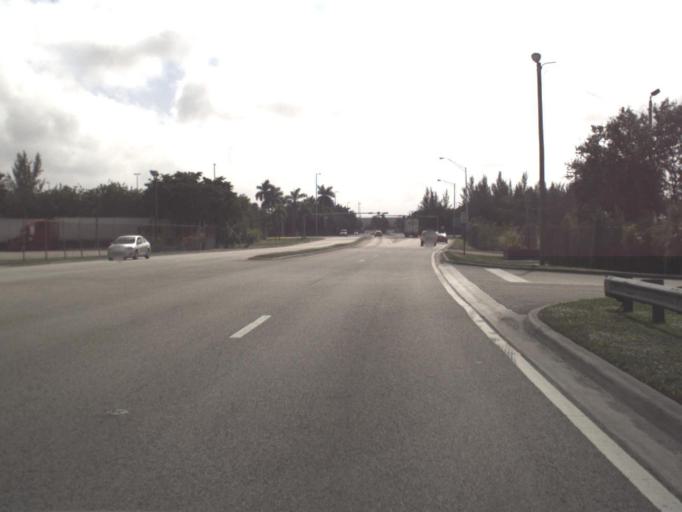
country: US
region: Florida
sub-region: Miami-Dade County
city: Virginia Gardens
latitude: 25.7993
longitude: -80.3066
